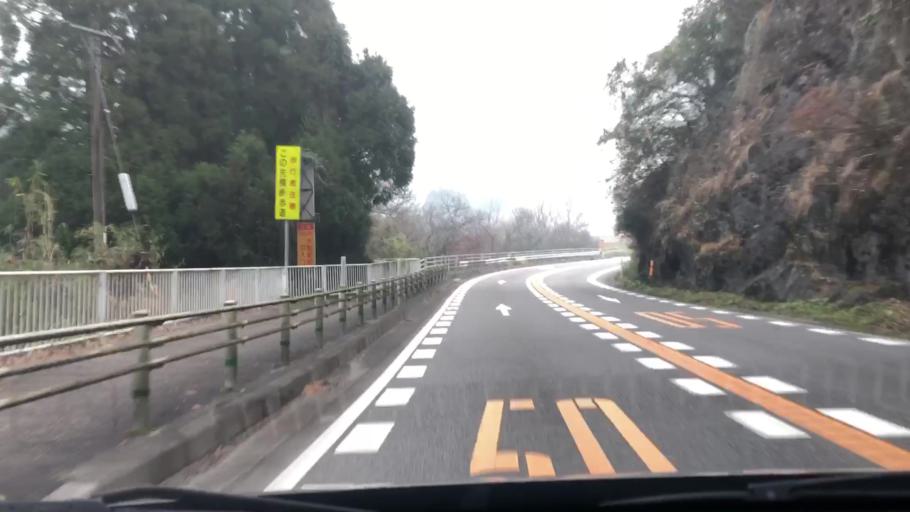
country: JP
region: Oita
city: Usuki
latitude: 33.0222
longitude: 131.6953
